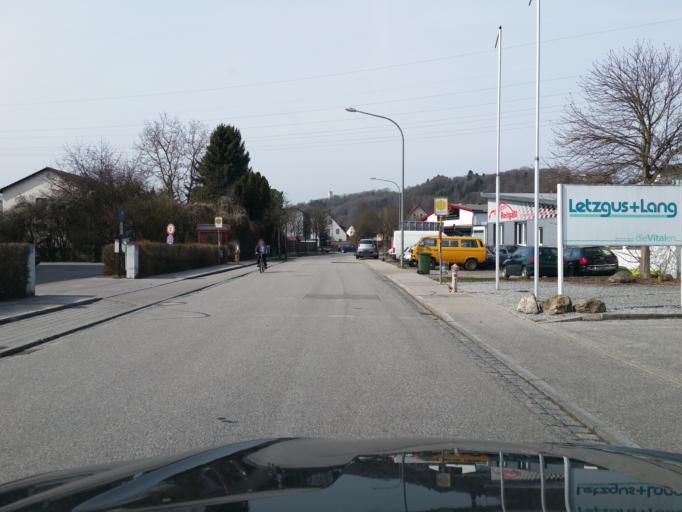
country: DE
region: Bavaria
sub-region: Lower Bavaria
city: Tiefenbach
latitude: 48.5490
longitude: 12.1015
